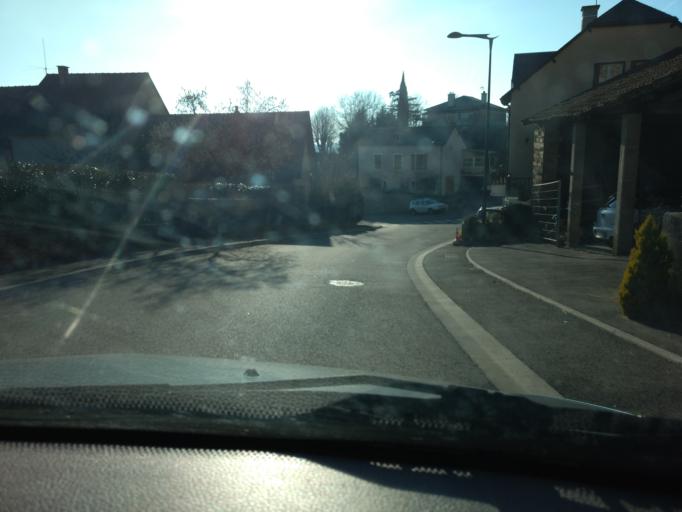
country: FR
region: Midi-Pyrenees
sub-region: Departement de l'Aveyron
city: Naucelle
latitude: 44.1963
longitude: 2.3407
